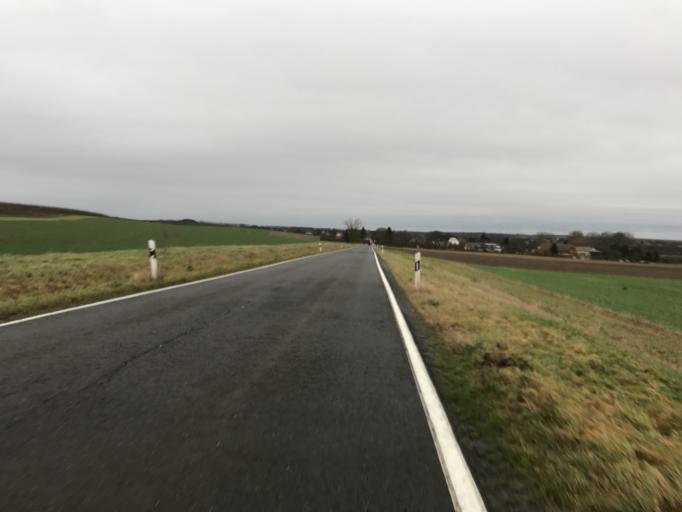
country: DE
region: Rheinland-Pfalz
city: Hahnheim
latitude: 49.8686
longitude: 8.2186
